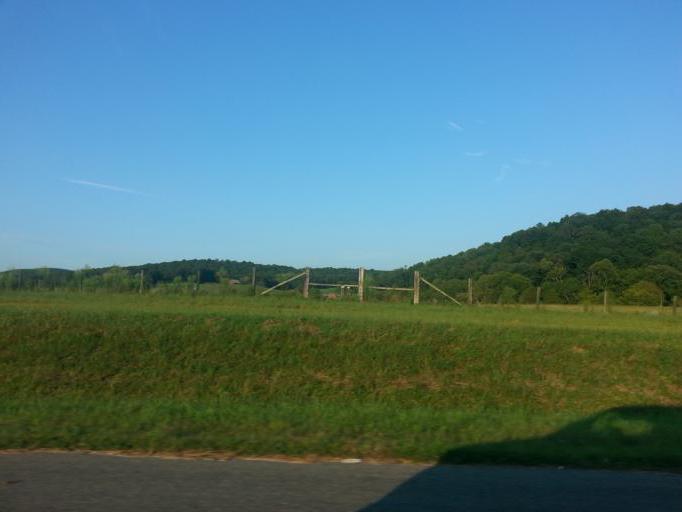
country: US
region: Tennessee
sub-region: McMinn County
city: Athens
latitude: 35.5444
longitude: -84.6625
